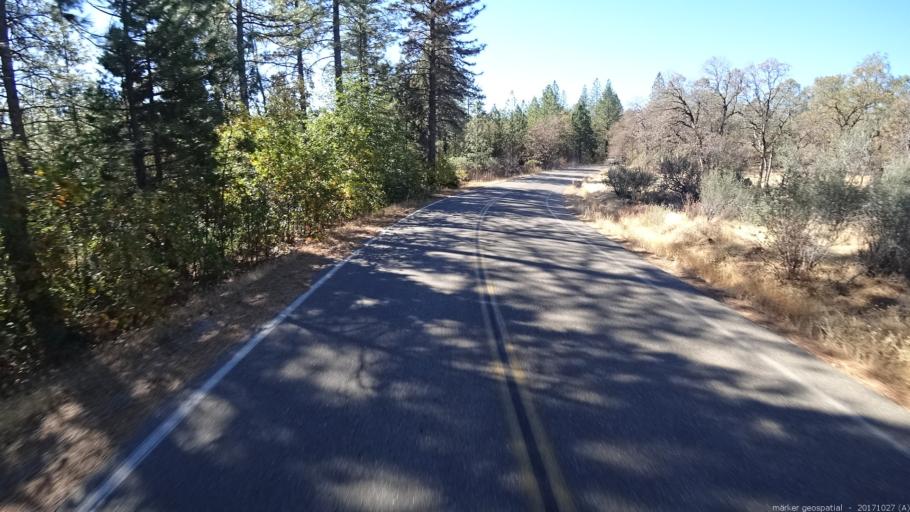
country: US
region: California
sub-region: Shasta County
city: Shingletown
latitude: 40.7004
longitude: -121.9881
